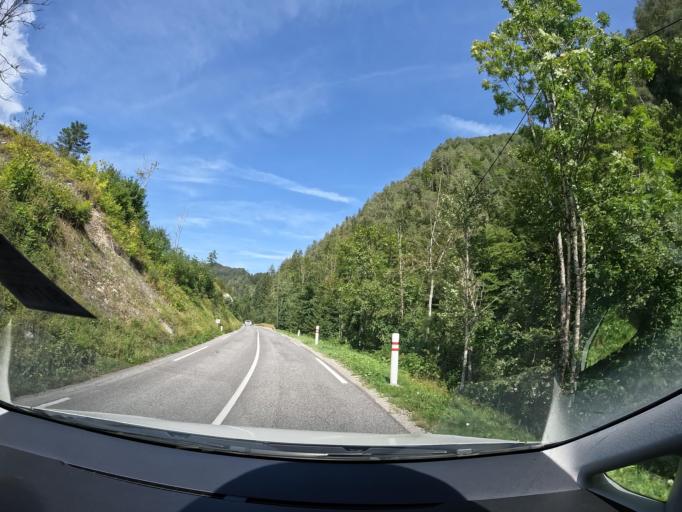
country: SI
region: Zirovnica
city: Zirovnica
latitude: 46.4262
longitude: 14.1327
